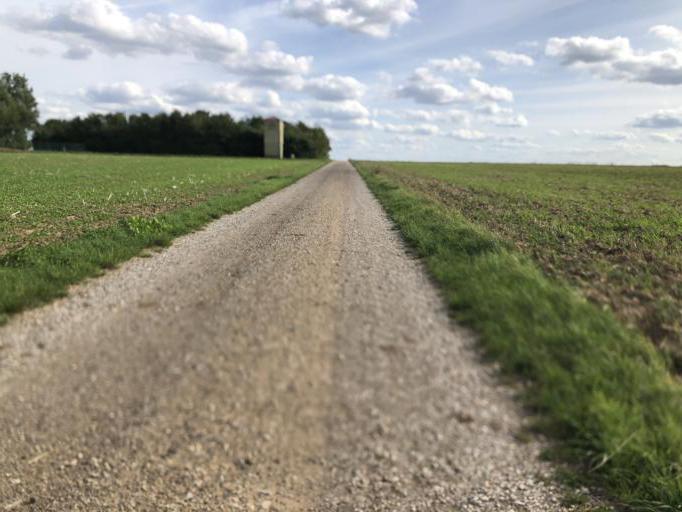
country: DE
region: Bavaria
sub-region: Regierungsbezirk Mittelfranken
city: Obermichelbach
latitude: 49.5434
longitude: 10.9415
